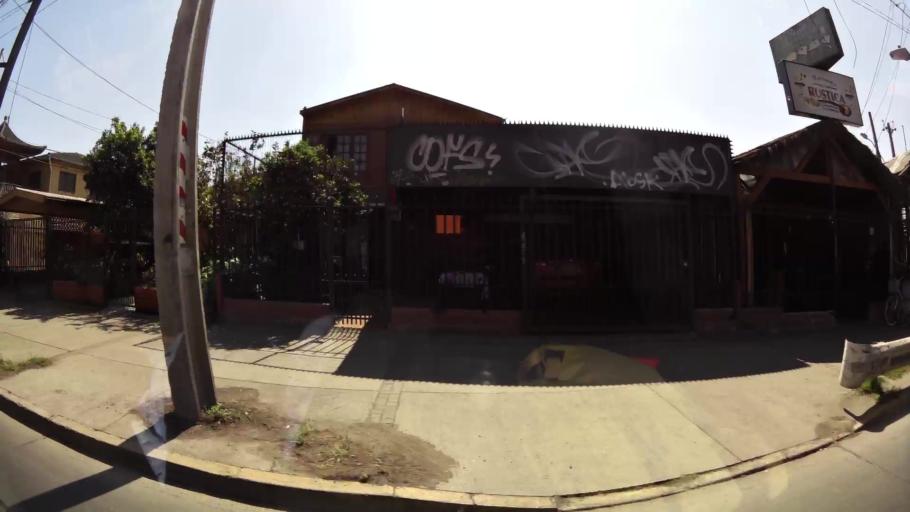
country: CL
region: Santiago Metropolitan
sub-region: Provincia de Santiago
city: Lo Prado
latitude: -33.3654
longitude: -70.7278
